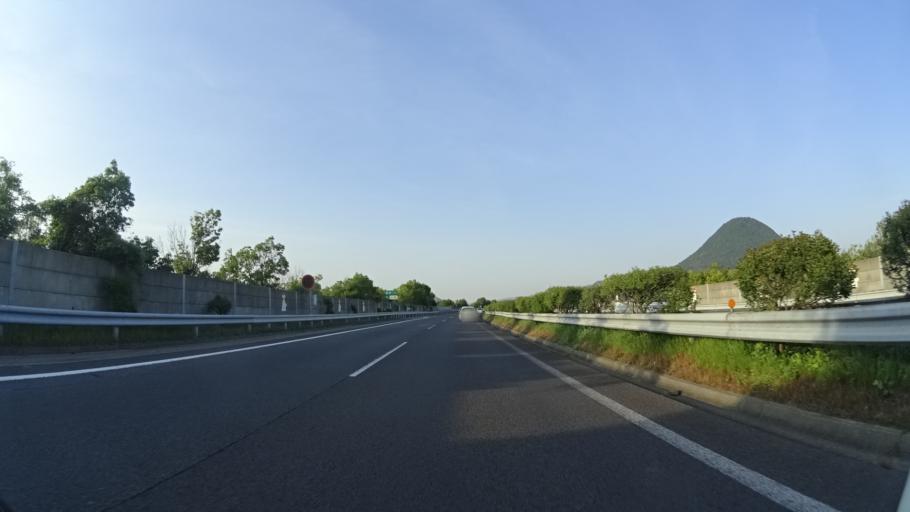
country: JP
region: Kagawa
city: Marugame
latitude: 34.2660
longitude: 133.8208
